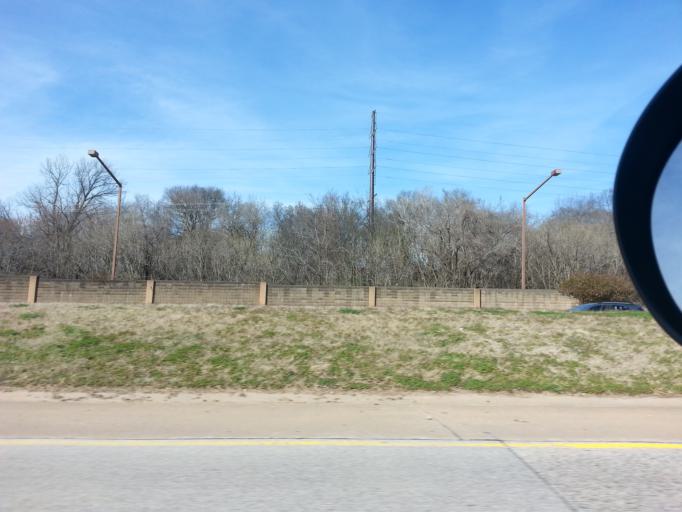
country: US
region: Tennessee
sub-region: Davidson County
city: Oak Hill
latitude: 36.1159
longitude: -86.7804
